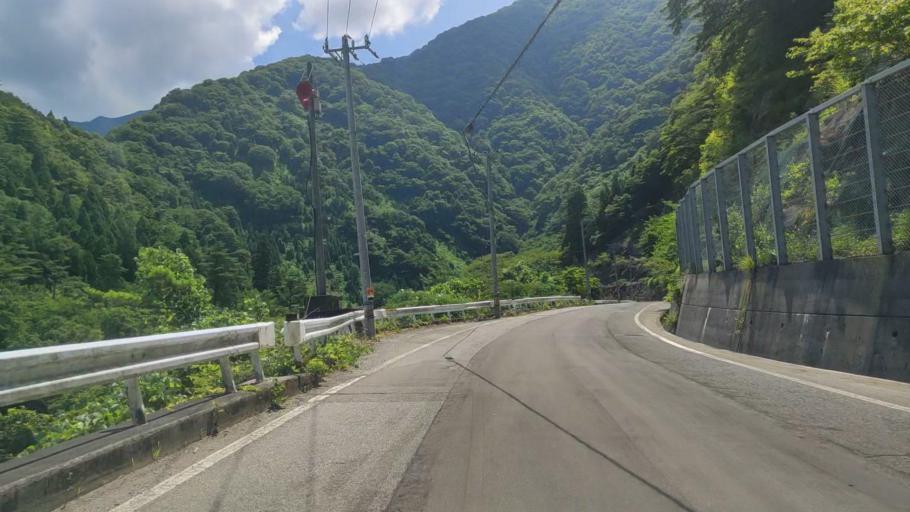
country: JP
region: Fukui
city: Ono
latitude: 35.9346
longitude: 136.5587
